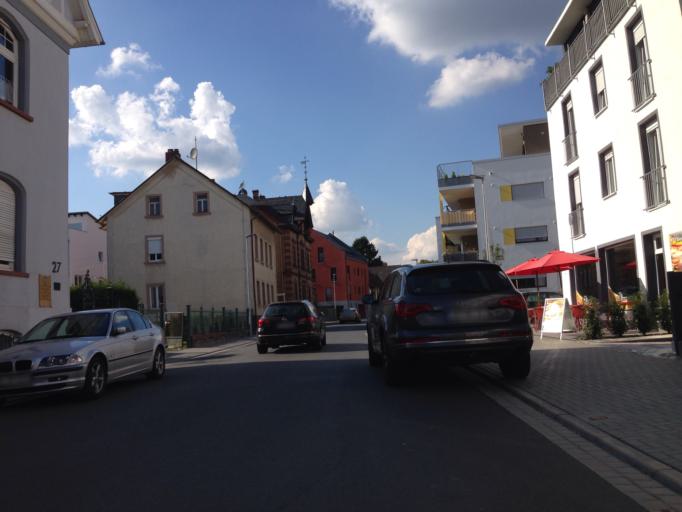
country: DE
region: Hesse
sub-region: Regierungsbezirk Darmstadt
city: Friedrichsdorf
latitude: 50.2532
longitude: 8.6423
